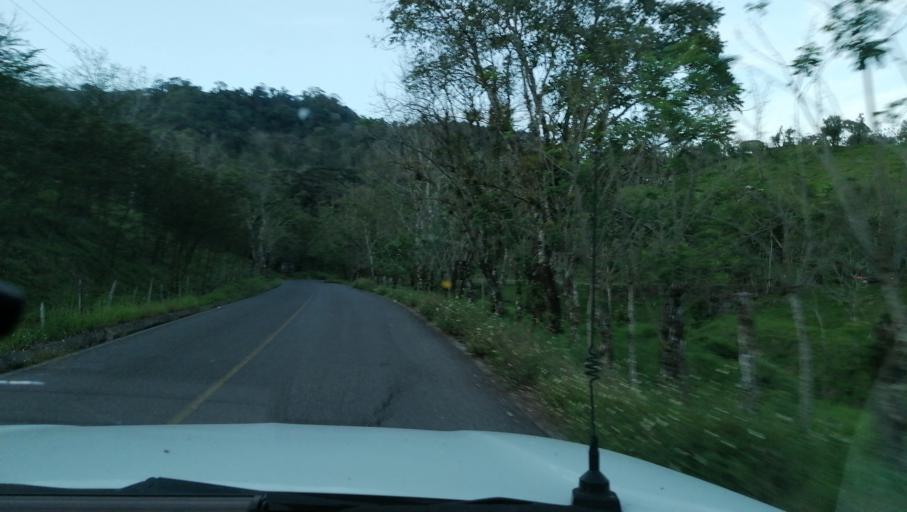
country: MX
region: Chiapas
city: Ostuacan
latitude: 17.4223
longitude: -93.3381
